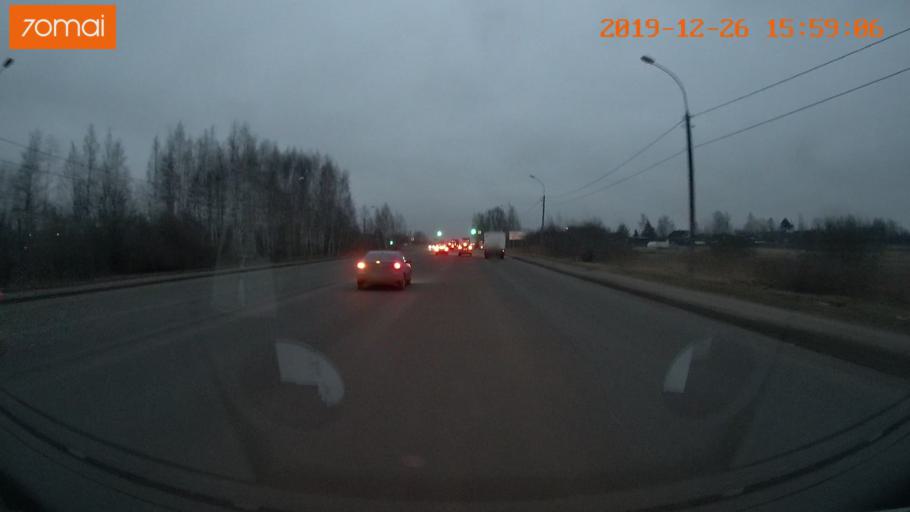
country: RU
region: Jaroslavl
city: Rybinsk
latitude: 58.0340
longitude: 38.8016
